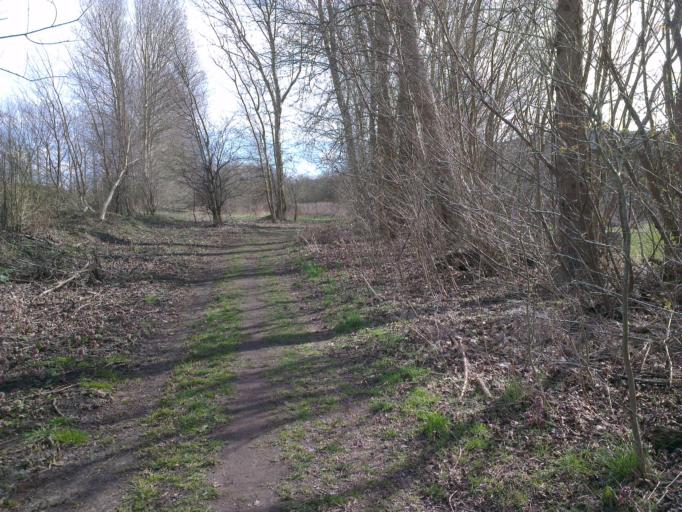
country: DK
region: Capital Region
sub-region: Frederikssund Kommune
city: Frederikssund
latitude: 55.8516
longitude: 12.0708
